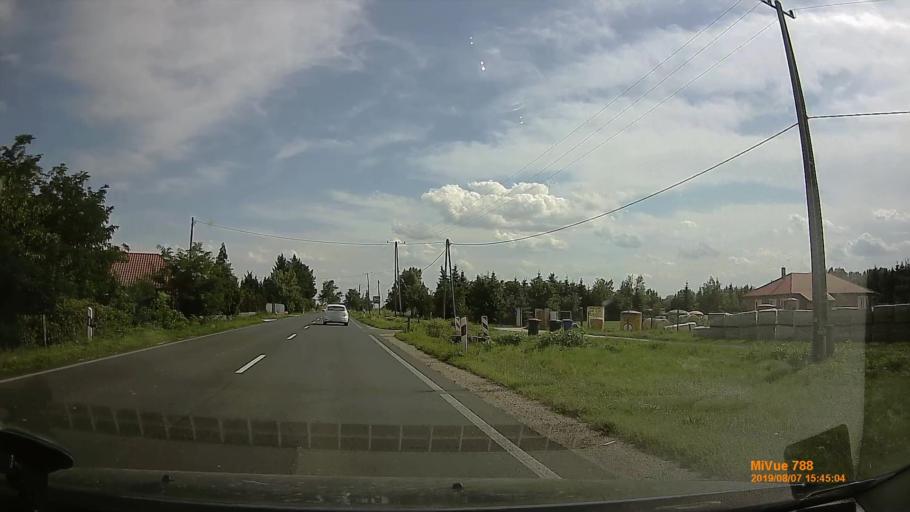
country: HU
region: Vas
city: Szombathely
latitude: 47.2023
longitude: 16.6183
